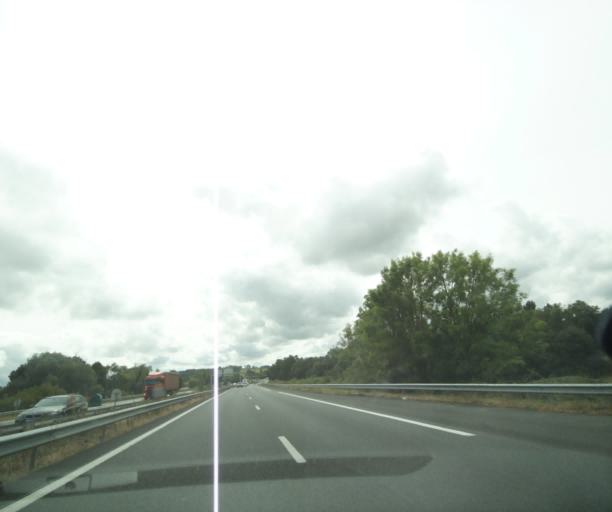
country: FR
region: Poitou-Charentes
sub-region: Departement de la Charente-Maritime
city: Mirambeau
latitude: 45.3701
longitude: -0.5924
